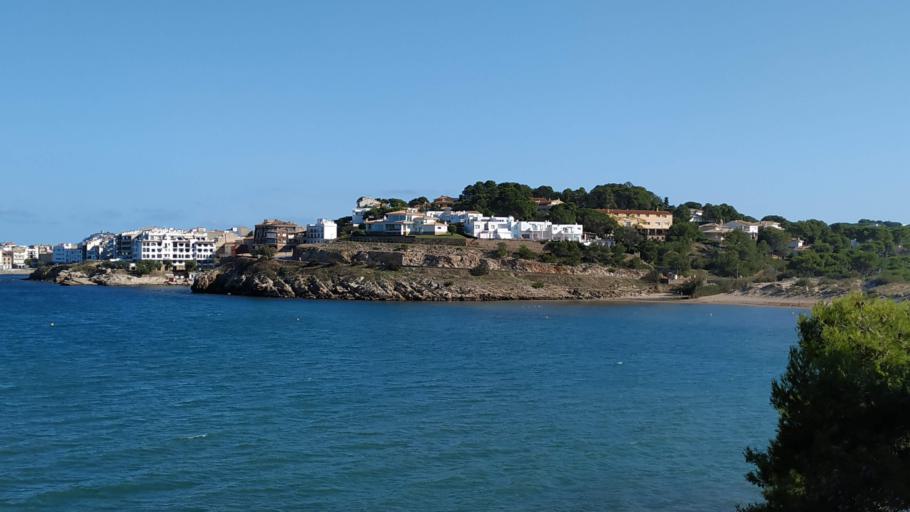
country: ES
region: Catalonia
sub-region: Provincia de Girona
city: l'Escala
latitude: 42.1296
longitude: 3.1238
